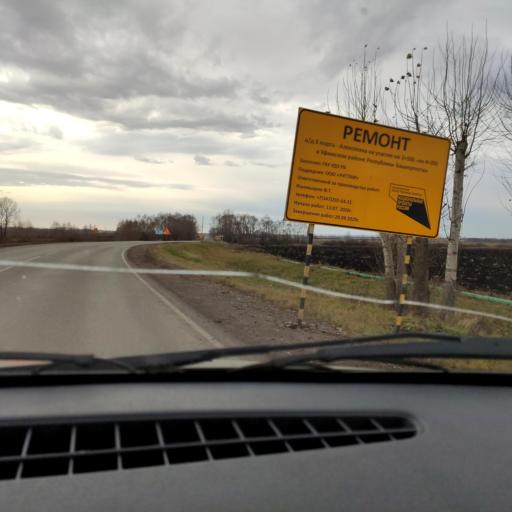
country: RU
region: Bashkortostan
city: Ufa
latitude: 54.8185
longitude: 55.9838
